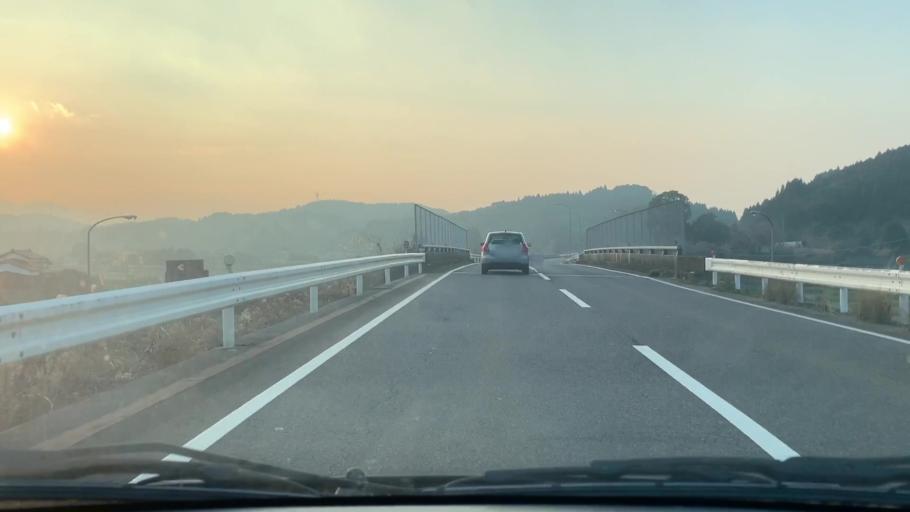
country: JP
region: Saga Prefecture
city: Imaricho-ko
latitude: 33.2640
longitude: 129.9632
